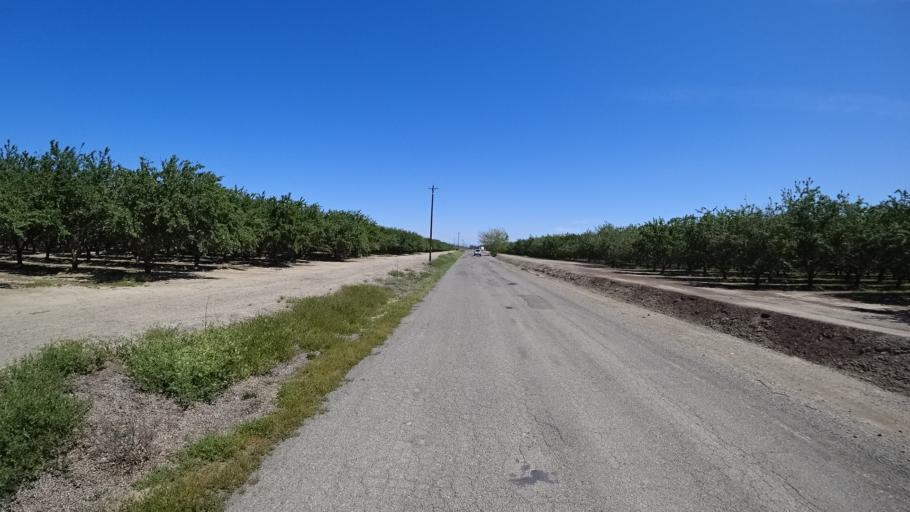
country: US
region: California
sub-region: Glenn County
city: Orland
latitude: 39.7323
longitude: -122.1363
